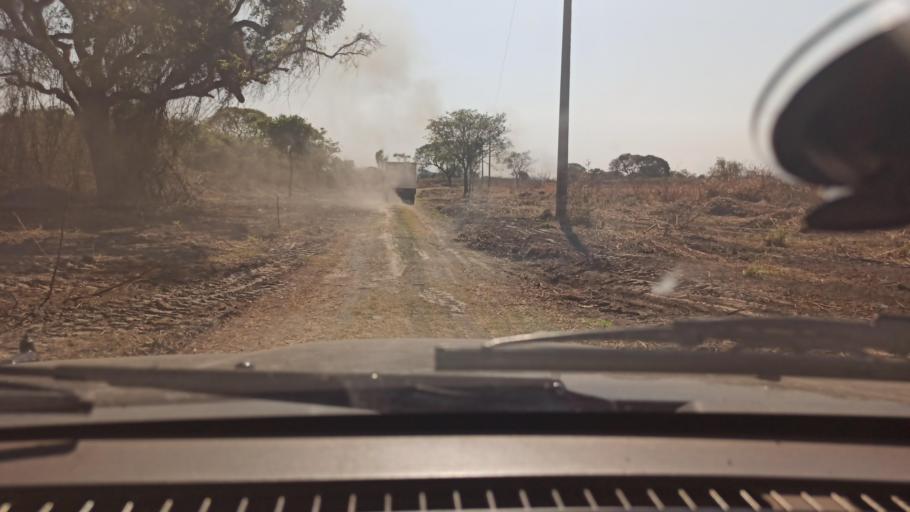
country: PY
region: Asuncion
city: Asuncion
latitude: -25.3447
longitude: -57.6756
